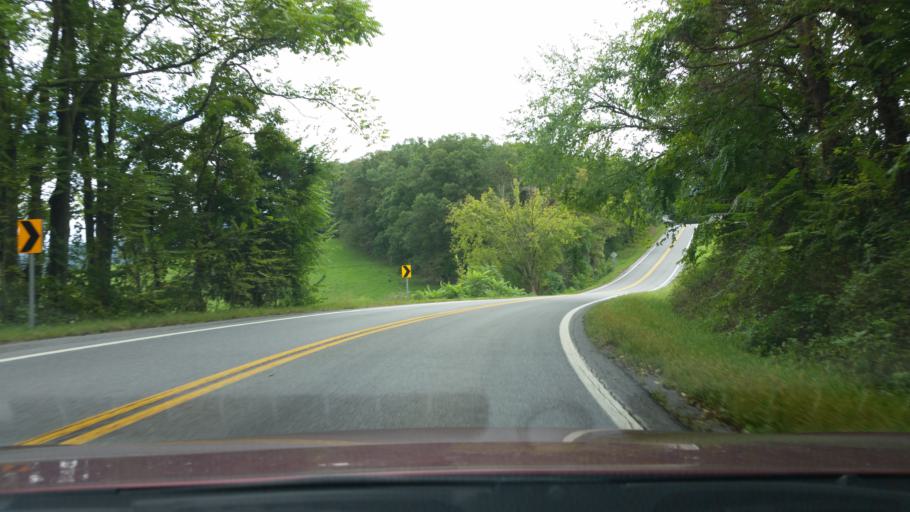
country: US
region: Maryland
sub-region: Washington County
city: Hancock
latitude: 39.6402
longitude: -78.1524
